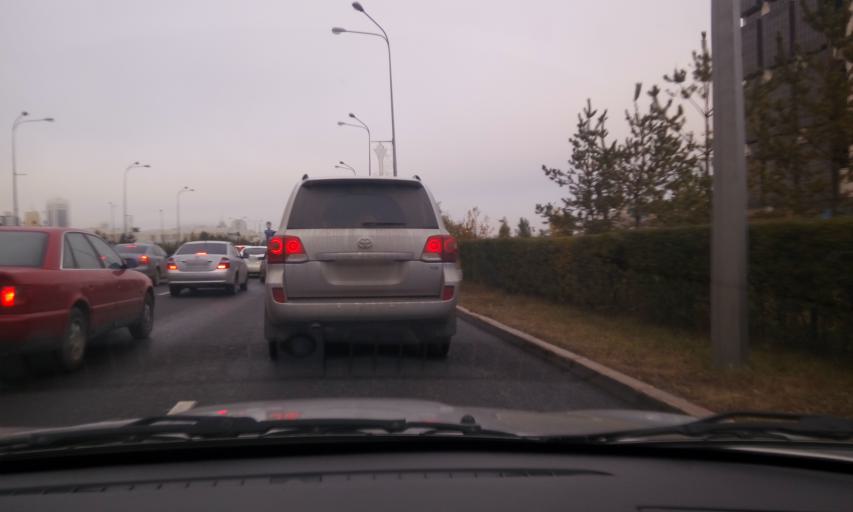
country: KZ
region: Astana Qalasy
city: Astana
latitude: 51.1293
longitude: 71.4605
